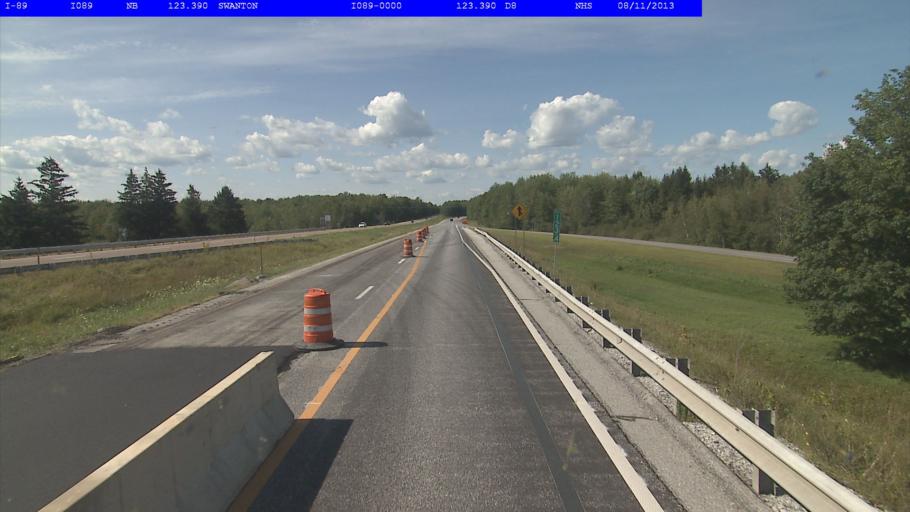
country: US
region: Vermont
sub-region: Franklin County
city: Swanton
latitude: 44.9226
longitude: -73.1075
